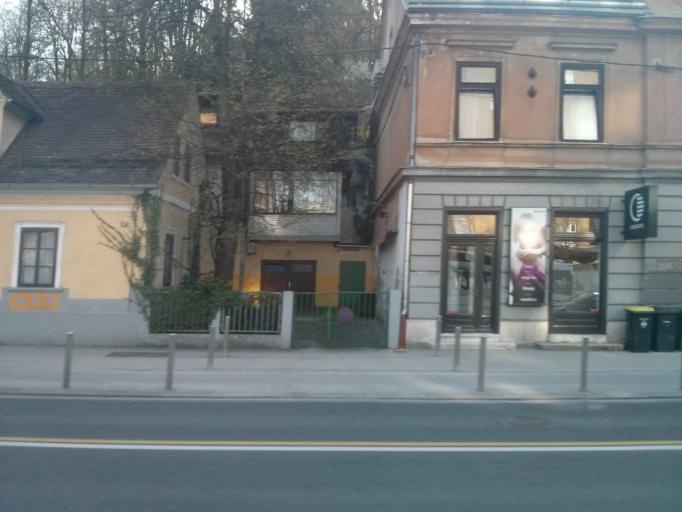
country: SI
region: Ljubljana
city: Ljubljana
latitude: 46.0619
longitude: 14.4958
